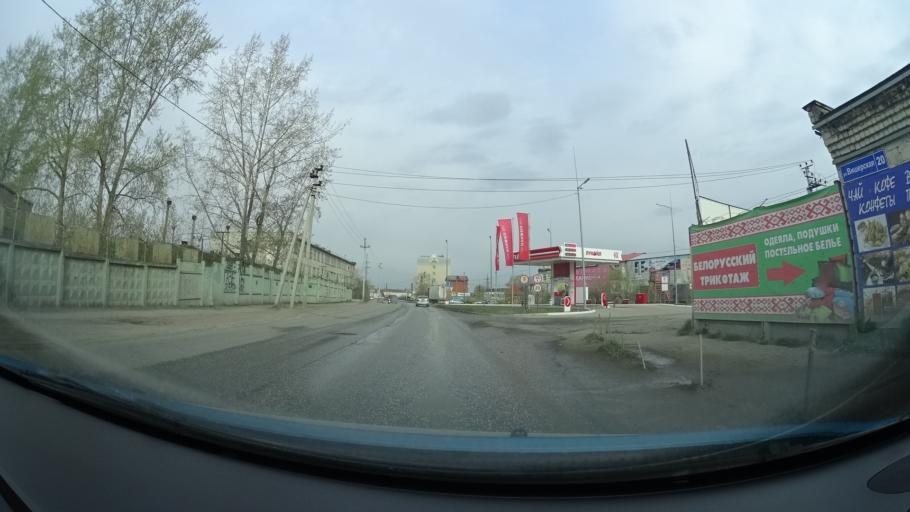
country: RU
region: Perm
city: Kondratovo
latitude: 58.0031
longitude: 56.1581
